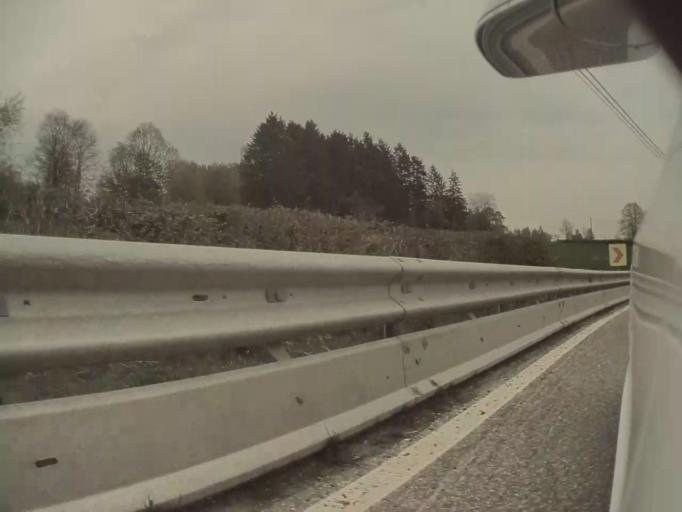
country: BE
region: Wallonia
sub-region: Province du Luxembourg
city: Manhay
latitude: 50.3815
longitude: 5.7110
